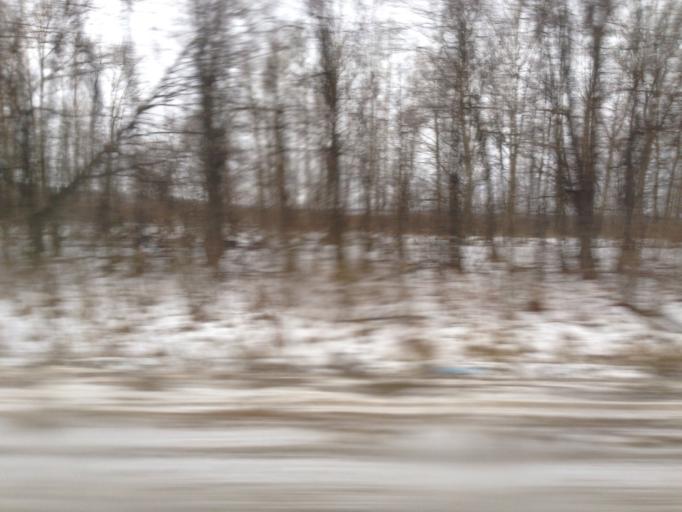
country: RU
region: Tula
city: Bolokhovo
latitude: 54.0846
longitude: 37.7771
